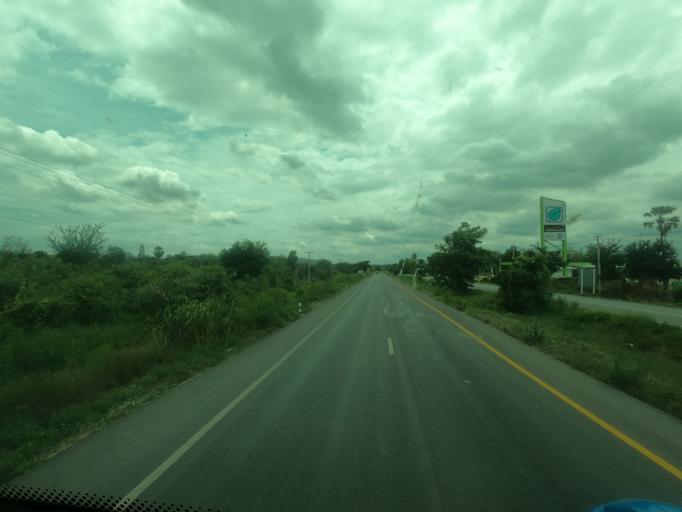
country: TH
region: Nakhon Ratchasima
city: Sikhio
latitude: 14.8509
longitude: 101.7138
